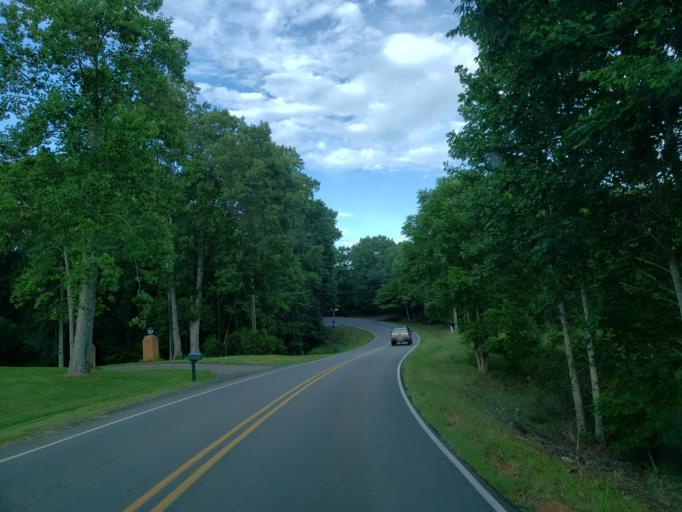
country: US
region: Georgia
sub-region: Cherokee County
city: Ball Ground
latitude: 34.3334
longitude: -84.4545
